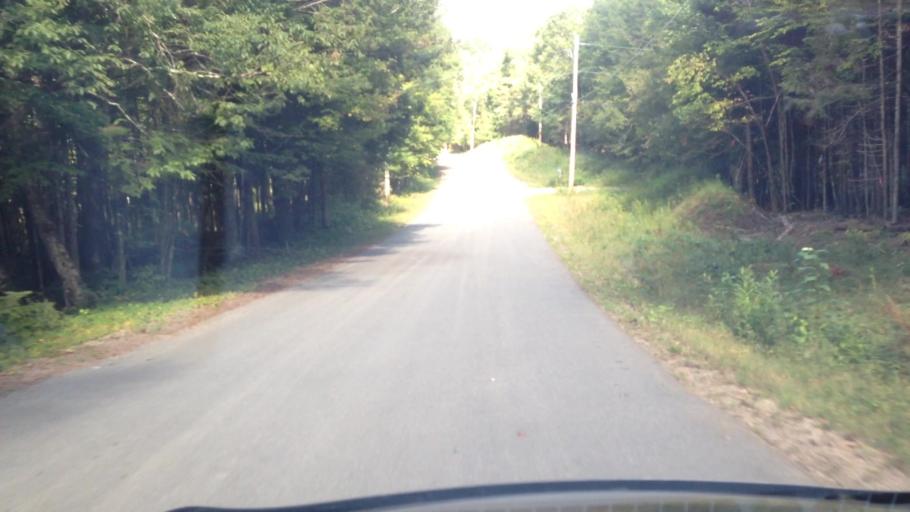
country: CA
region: Quebec
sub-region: Laurentides
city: Mont-Tremblant
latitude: 45.9433
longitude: -74.5887
